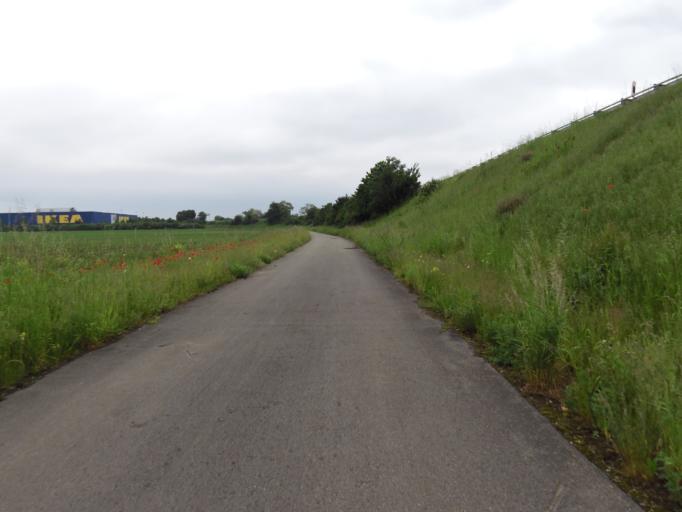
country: DE
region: Hesse
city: Lampertheim
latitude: 49.5534
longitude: 8.4397
